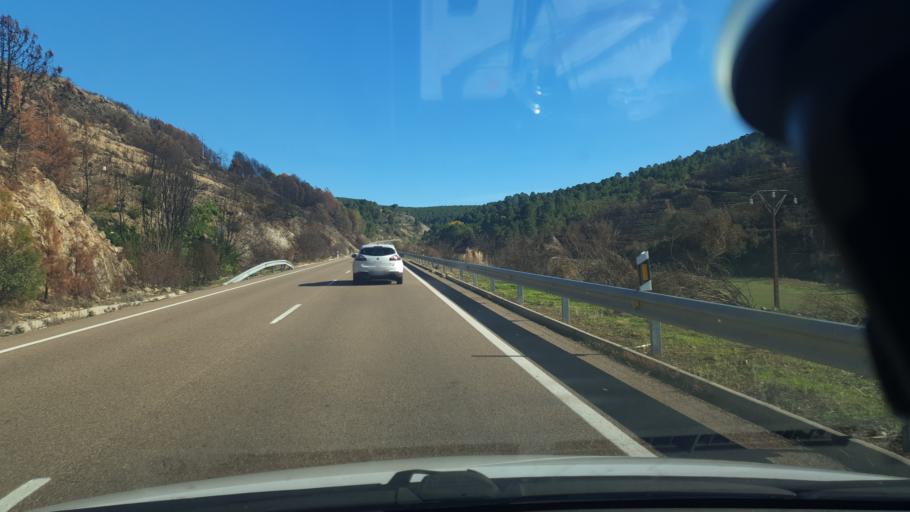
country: ES
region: Castille and Leon
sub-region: Provincia de Avila
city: Poyales del Hoyo
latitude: 40.1645
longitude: -5.1399
